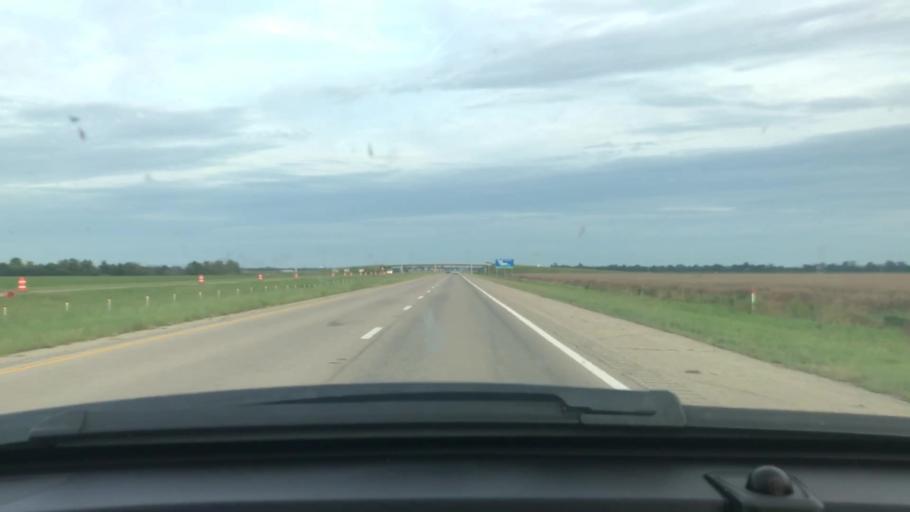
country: US
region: Arkansas
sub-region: Craighead County
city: Bay
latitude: 35.7097
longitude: -90.5717
